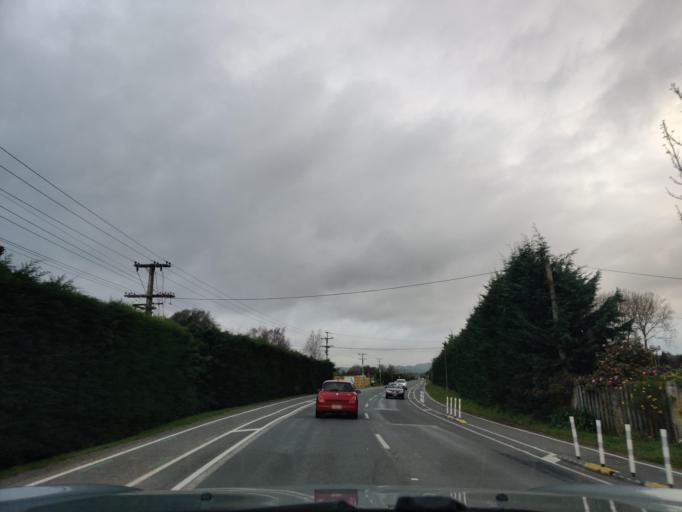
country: NZ
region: Hawke's Bay
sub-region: Hastings District
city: Hastings
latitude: -39.6352
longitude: 176.8930
